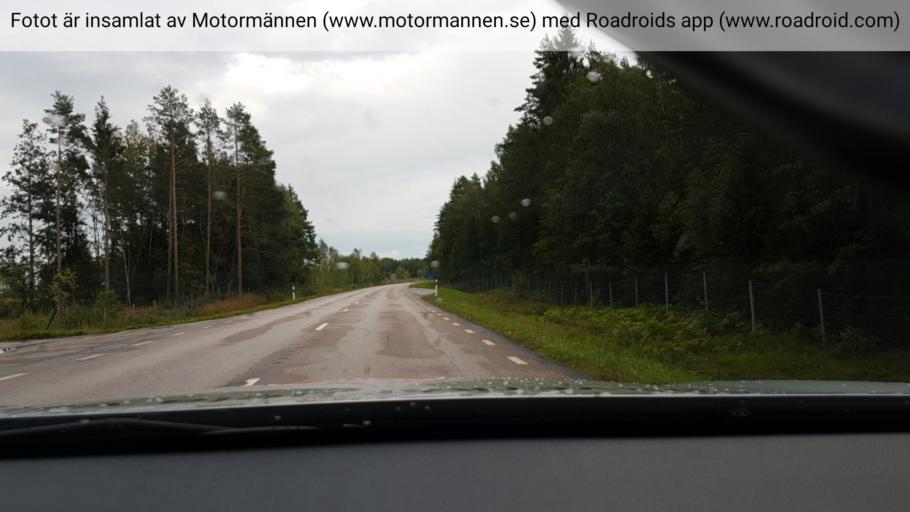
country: SE
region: Uppsala
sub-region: Osthammars Kommun
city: Osterbybruk
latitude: 60.4252
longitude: 17.8411
